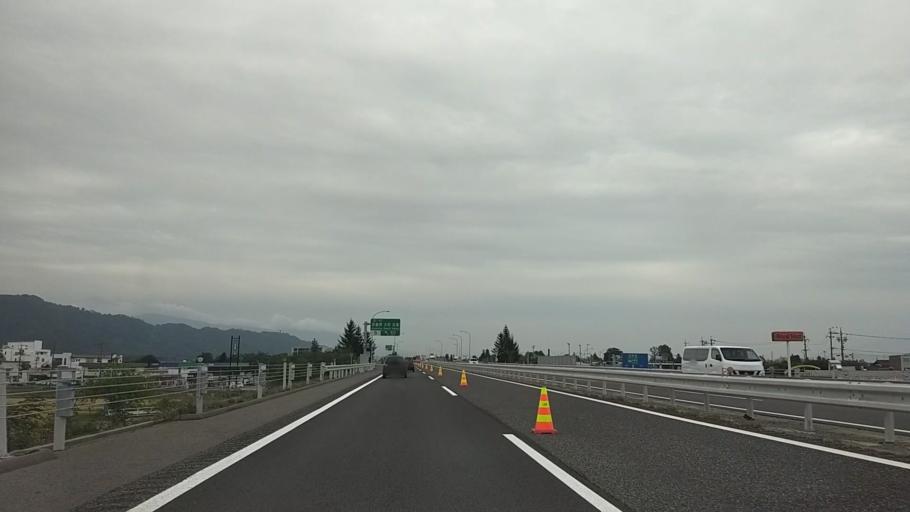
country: JP
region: Nagano
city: Toyoshina
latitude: 36.3024
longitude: 137.9237
